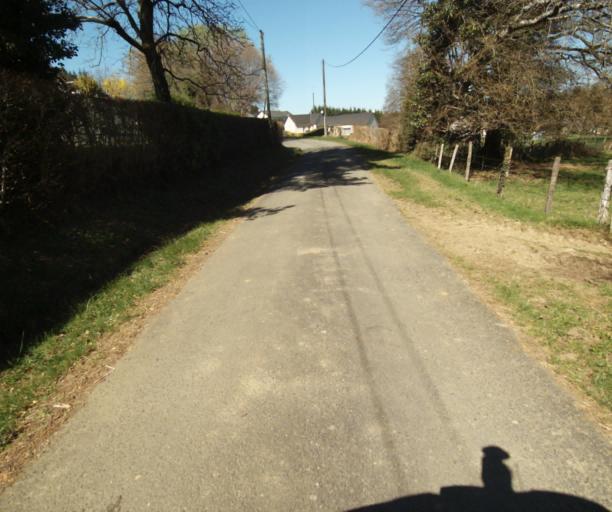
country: FR
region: Limousin
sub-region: Departement de la Correze
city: Saint-Clement
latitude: 45.3944
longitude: 1.6444
